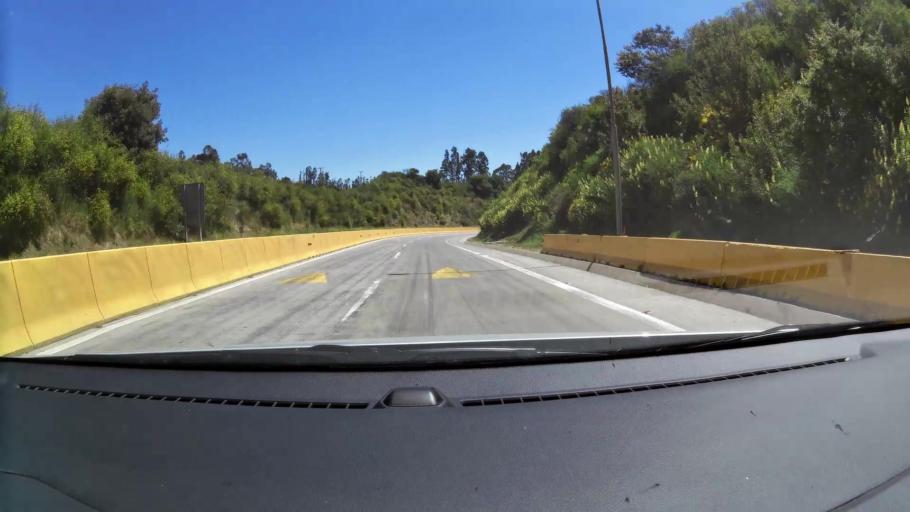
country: CL
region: Valparaiso
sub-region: Provincia de Valparaiso
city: Valparaiso
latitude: -33.0668
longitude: -71.6396
